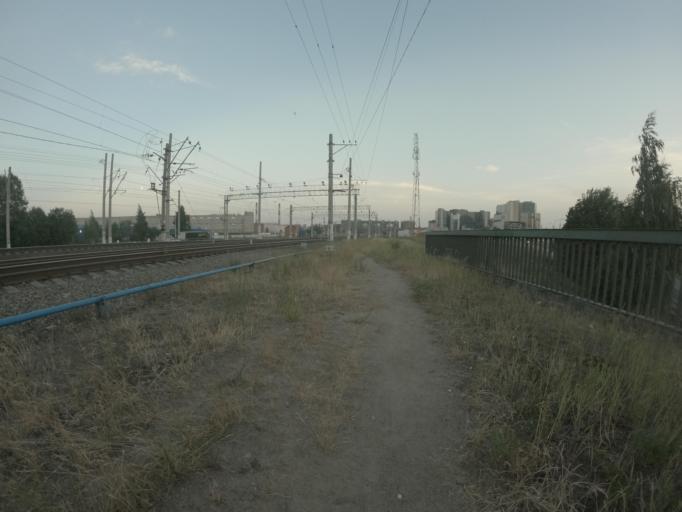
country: RU
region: St.-Petersburg
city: Krasnogvargeisky
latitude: 59.9364
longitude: 30.4468
